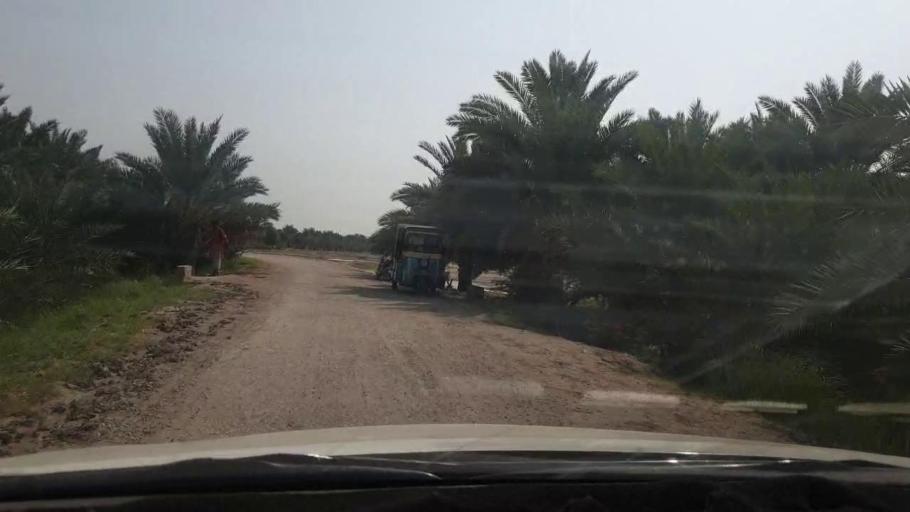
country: PK
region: Sindh
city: Rohri
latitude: 27.6122
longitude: 68.8973
